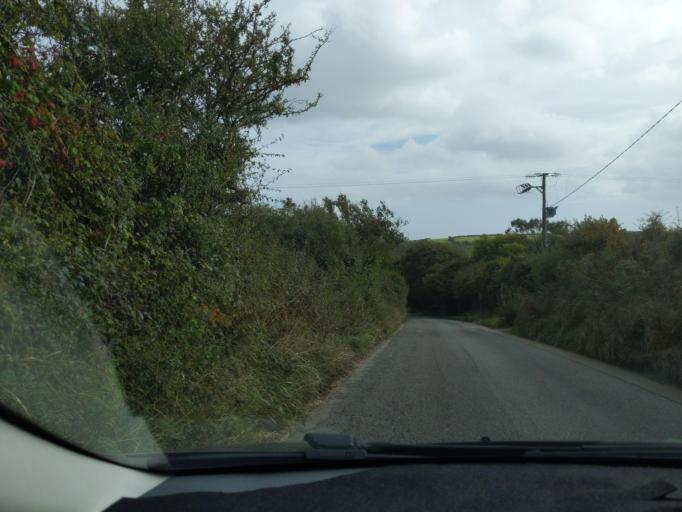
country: GB
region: England
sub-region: Cornwall
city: Mevagissey
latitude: 50.2432
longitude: -4.7999
